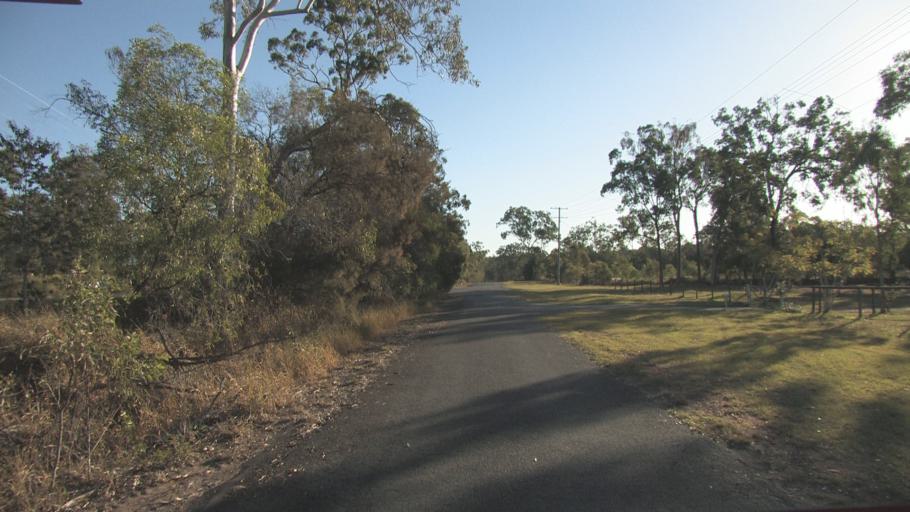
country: AU
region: Queensland
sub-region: Logan
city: Chambers Flat
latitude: -27.8044
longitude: 153.0701
